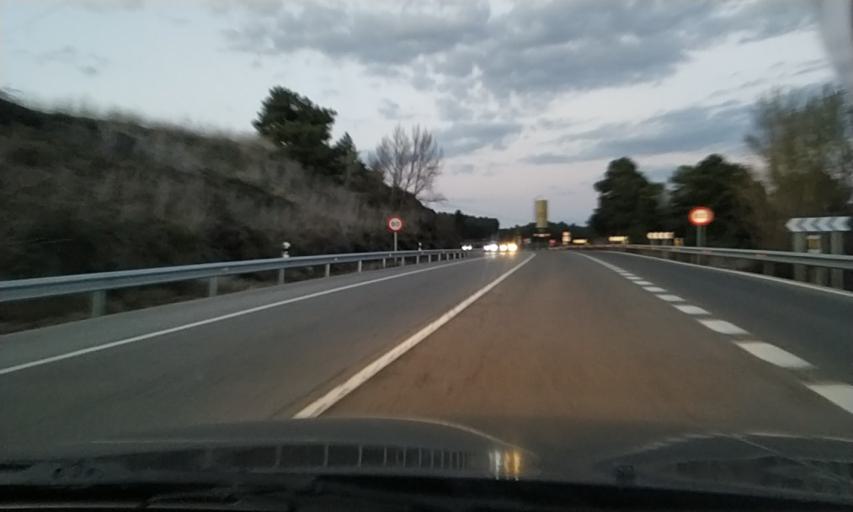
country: ES
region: Castille and Leon
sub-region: Provincia de Leon
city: Ponferrada
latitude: 42.5536
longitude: -6.5636
